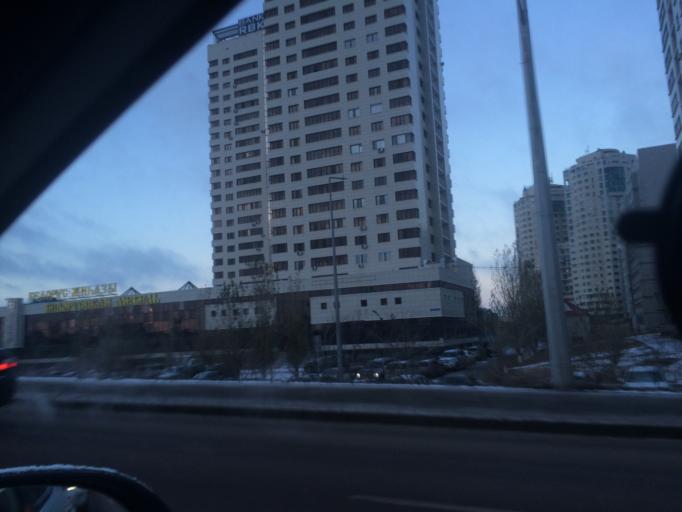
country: KZ
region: Astana Qalasy
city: Astana
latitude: 51.1596
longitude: 71.4107
